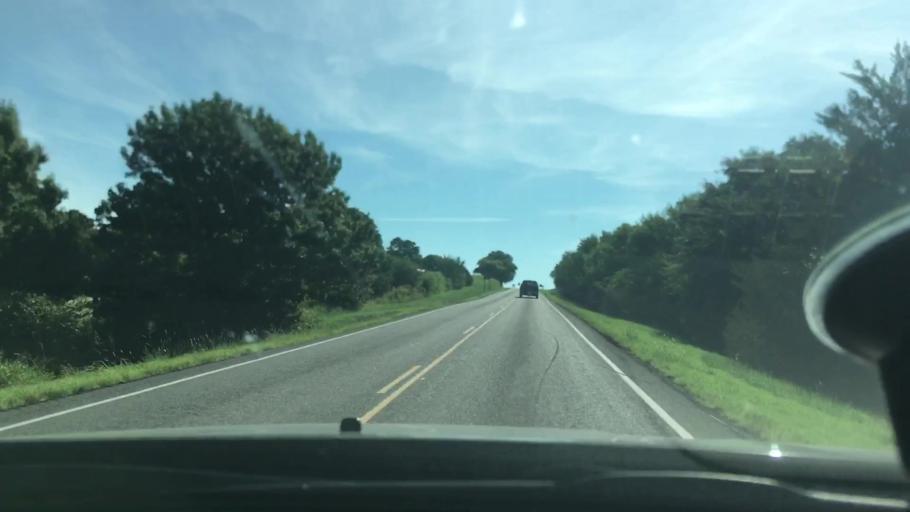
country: US
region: Oklahoma
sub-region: Carter County
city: Lone Grove
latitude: 34.3327
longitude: -97.2266
